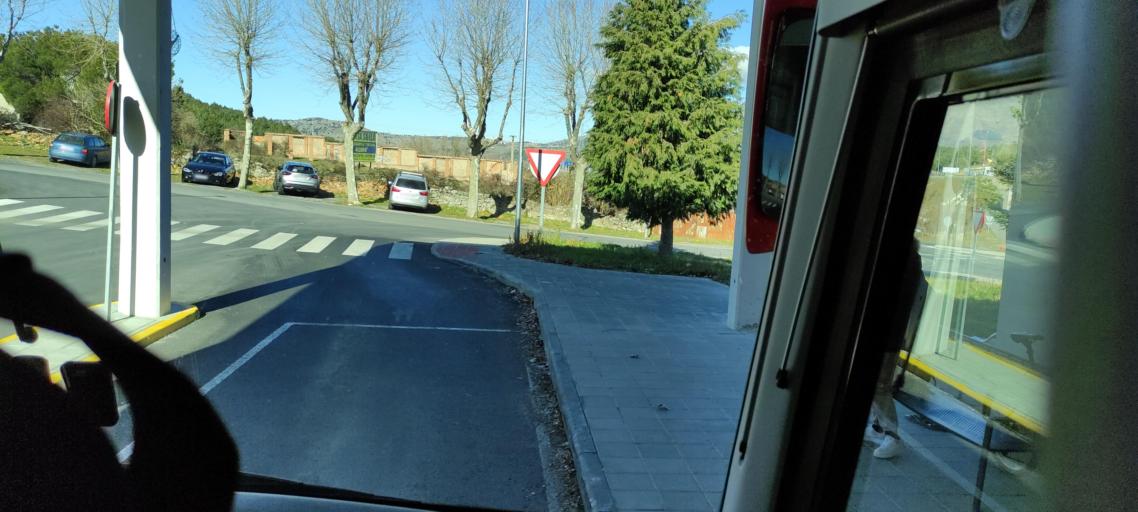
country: ES
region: Castille and Leon
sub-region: Provincia de Segovia
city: Otero de Herreros
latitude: 40.7204
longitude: -4.1926
